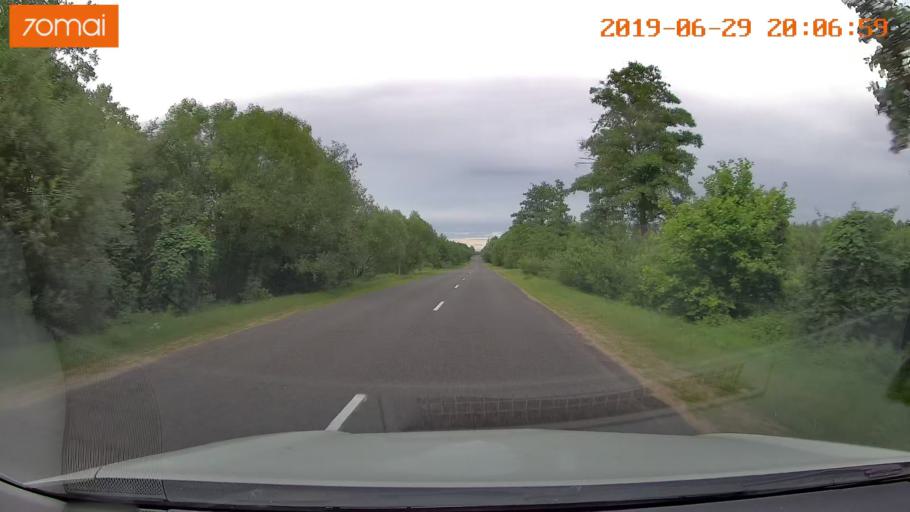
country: BY
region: Brest
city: Lahishyn
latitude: 52.3400
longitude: 26.0253
